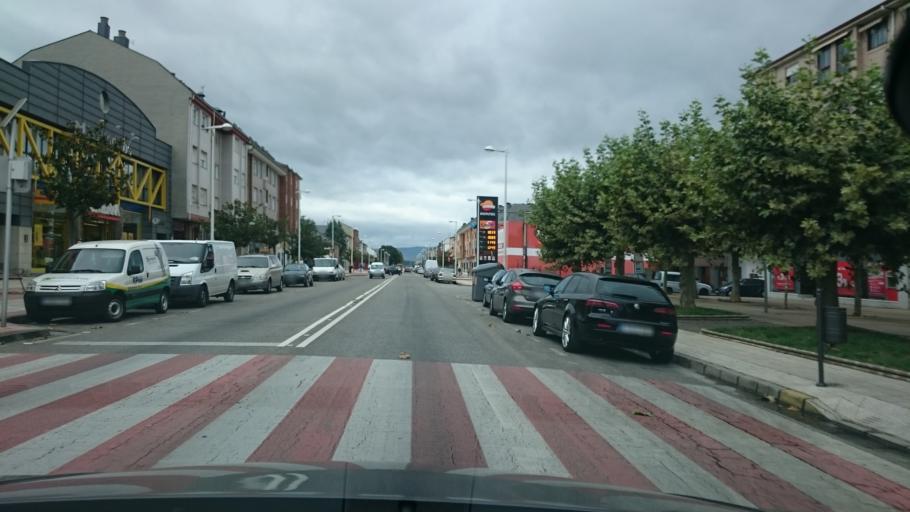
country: ES
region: Castille and Leon
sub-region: Provincia de Leon
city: Ponferrada
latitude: 42.5602
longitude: -6.6250
